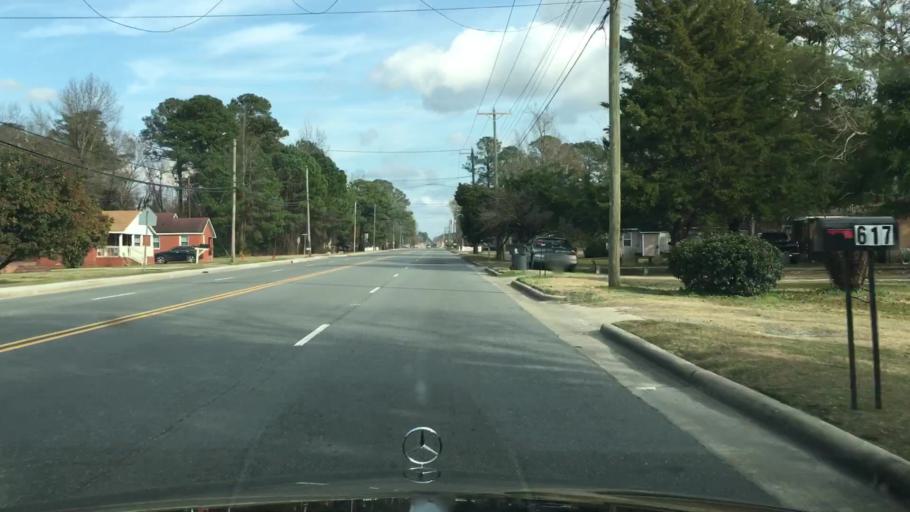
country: US
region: North Carolina
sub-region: Duplin County
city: Warsaw
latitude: 34.9956
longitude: -78.1057
